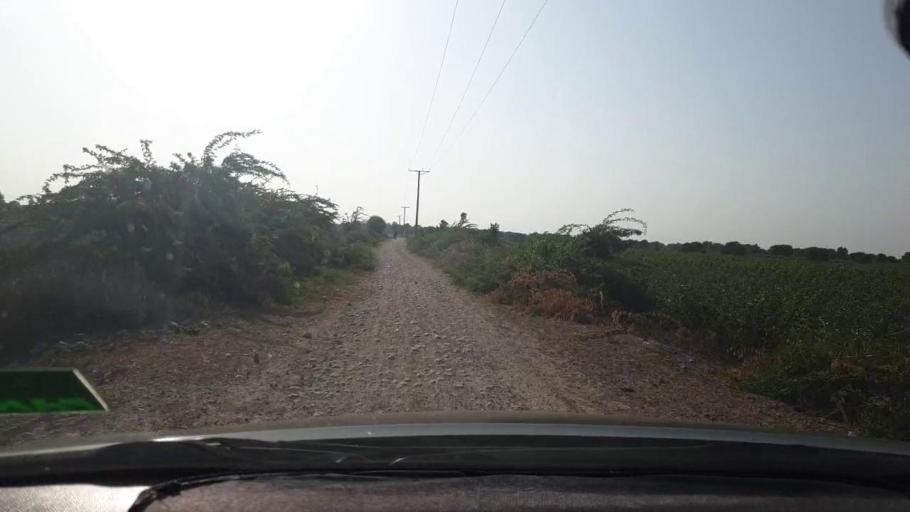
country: PK
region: Sindh
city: Naukot
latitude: 24.9032
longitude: 69.2736
